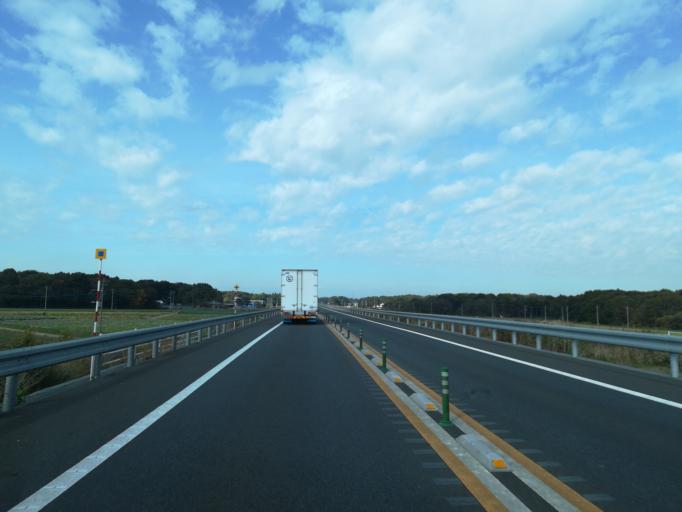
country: JP
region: Ibaraki
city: Iwai
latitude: 36.0989
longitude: 139.8681
